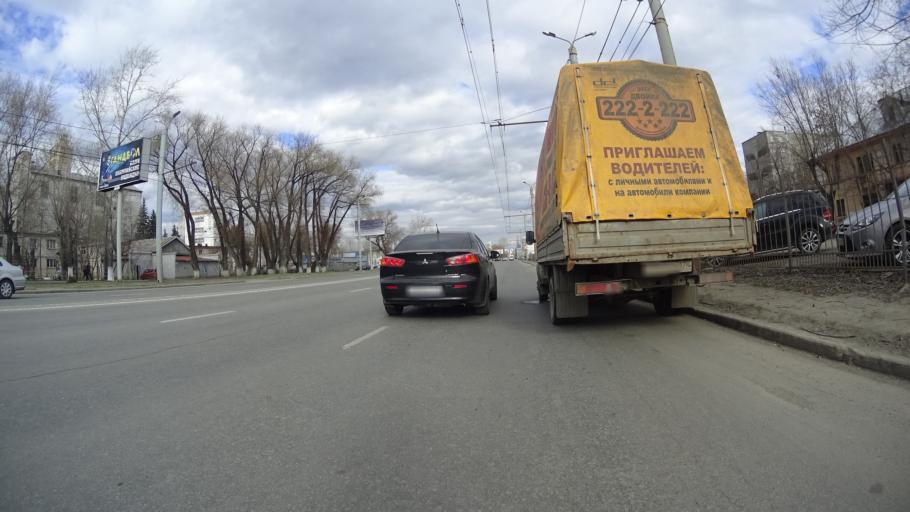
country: RU
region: Chelyabinsk
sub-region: Gorod Chelyabinsk
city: Chelyabinsk
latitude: 55.1675
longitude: 61.3839
